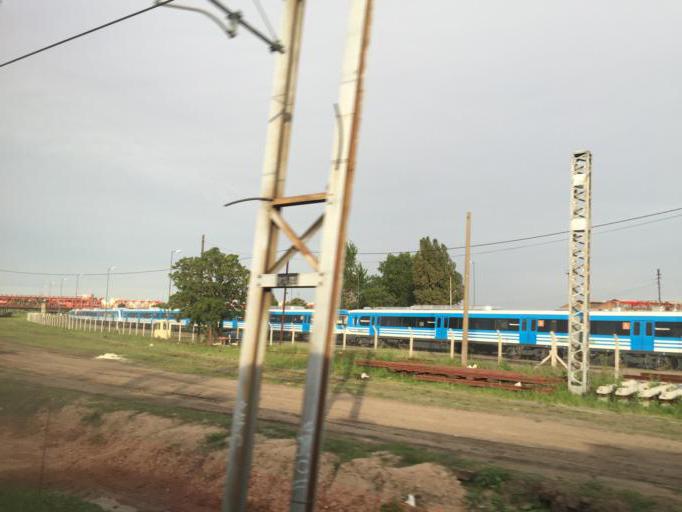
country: AR
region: Buenos Aires
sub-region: Partido de Avellaneda
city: Avellaneda
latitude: -34.6768
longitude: -58.3791
